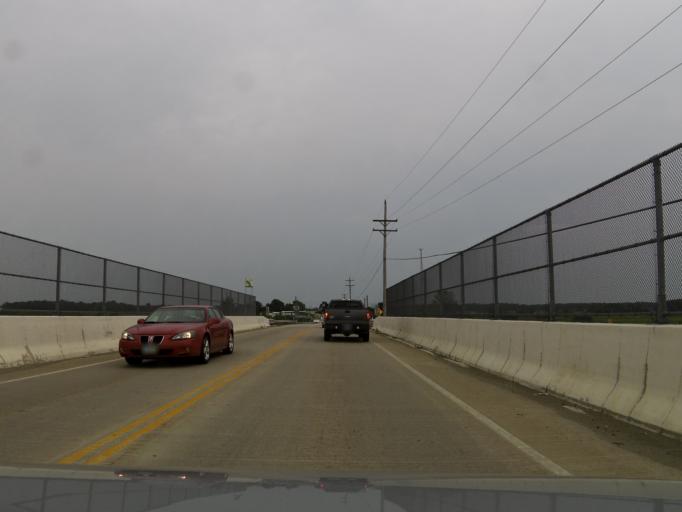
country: US
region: Ohio
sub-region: Clinton County
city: Wilmington
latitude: 39.4858
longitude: -83.9420
